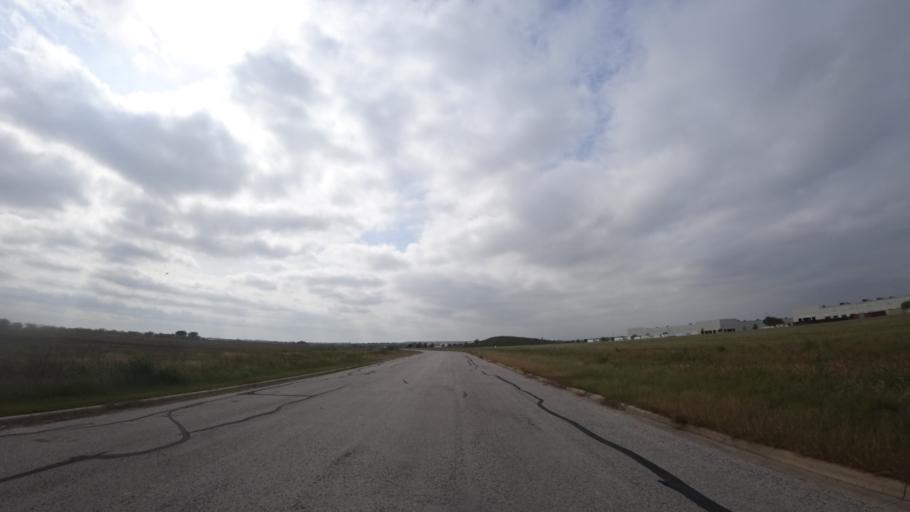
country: US
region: Texas
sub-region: Travis County
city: Manor
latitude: 30.3741
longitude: -97.6065
